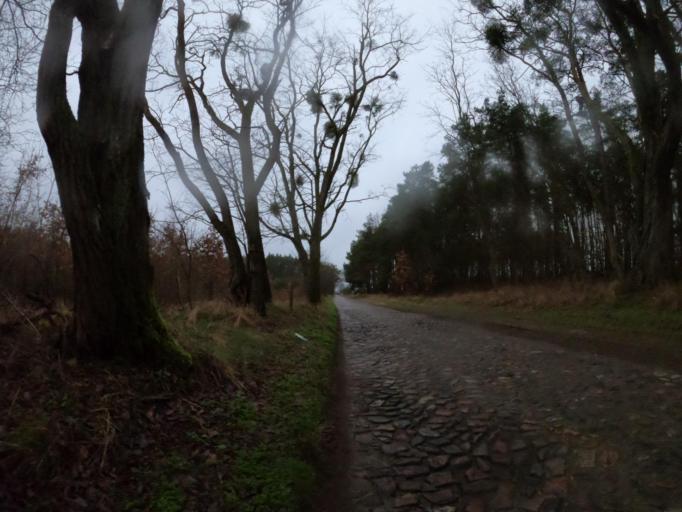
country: PL
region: West Pomeranian Voivodeship
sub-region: Powiat mysliborski
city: Debno
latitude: 52.8121
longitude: 14.7324
